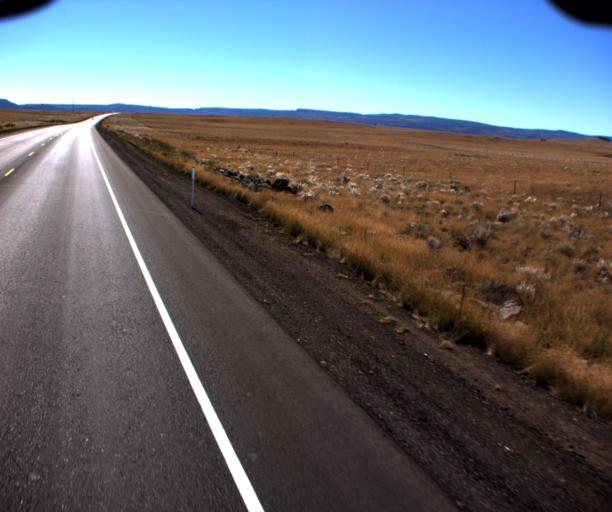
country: US
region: Arizona
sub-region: Apache County
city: Springerville
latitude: 34.1923
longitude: -109.3217
